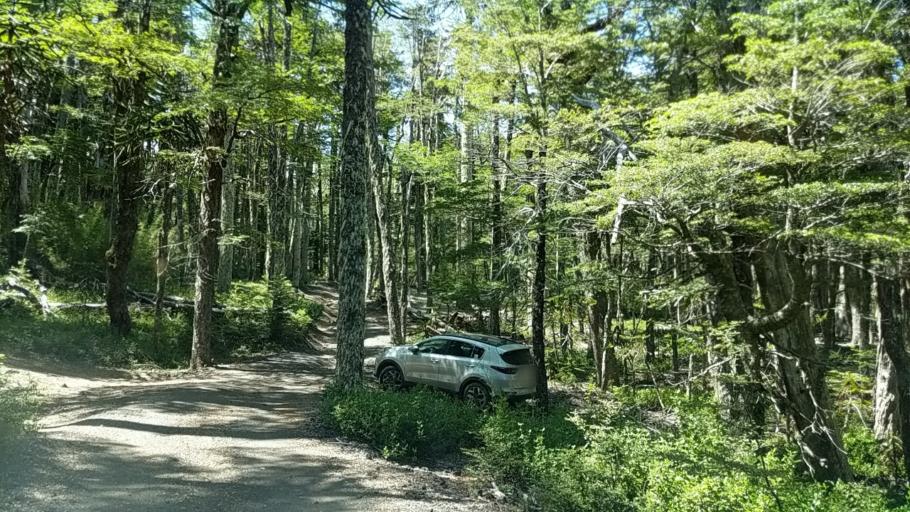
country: CL
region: Araucania
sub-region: Provincia de Cautin
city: Pucon
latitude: -39.4658
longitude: -71.8526
